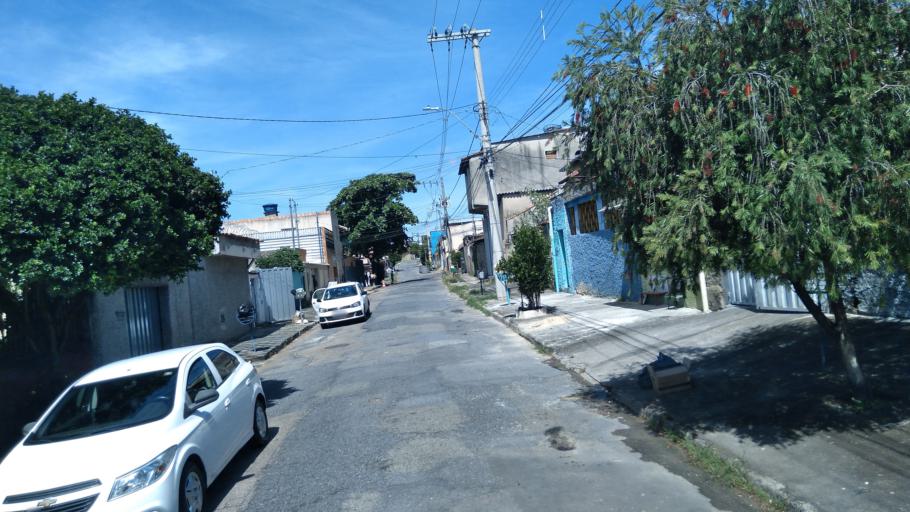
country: BR
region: Minas Gerais
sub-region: Contagem
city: Contagem
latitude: -19.8930
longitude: -44.0104
